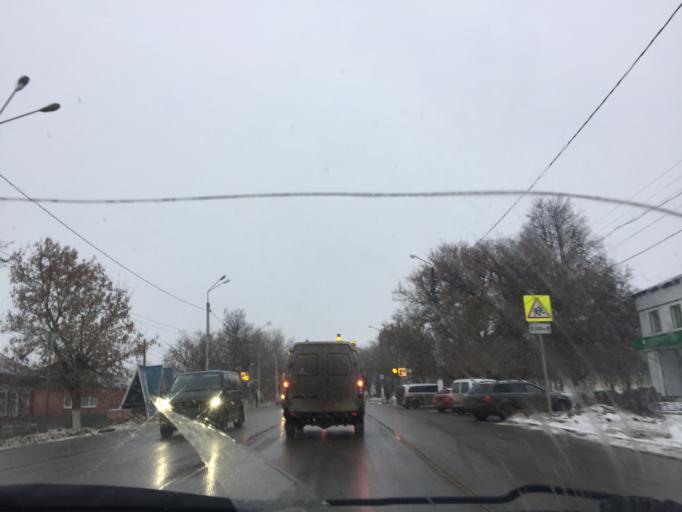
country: RU
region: Tula
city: Plavsk
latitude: 53.7048
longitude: 37.2901
